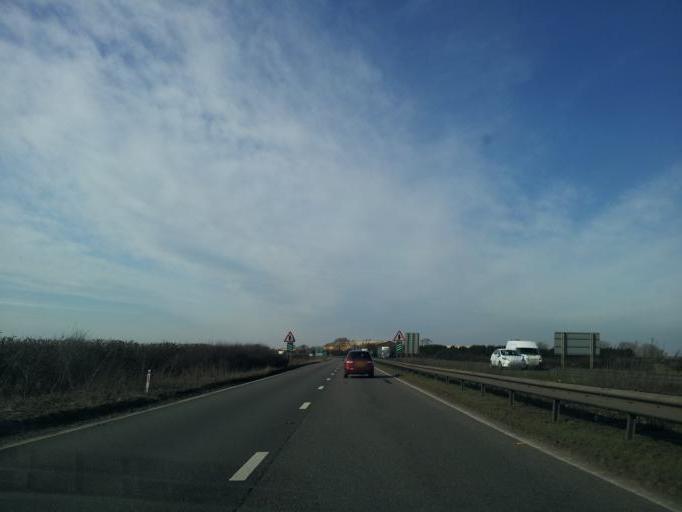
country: GB
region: England
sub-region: Lincolnshire
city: Great Gonerby
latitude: 52.9604
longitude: -0.6894
